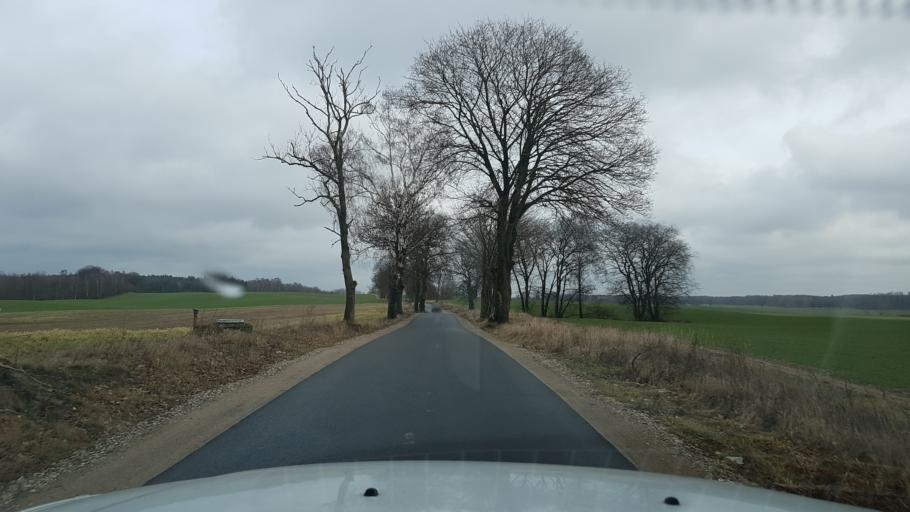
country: PL
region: West Pomeranian Voivodeship
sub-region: Powiat szczecinecki
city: Szczecinek
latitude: 53.7092
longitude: 16.7486
